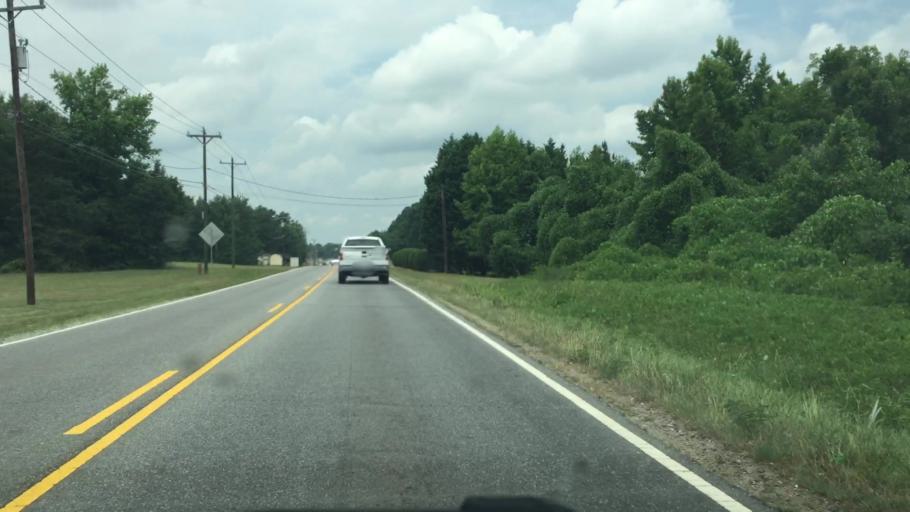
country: US
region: North Carolina
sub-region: Iredell County
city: Troutman
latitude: 35.6849
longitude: -80.8629
